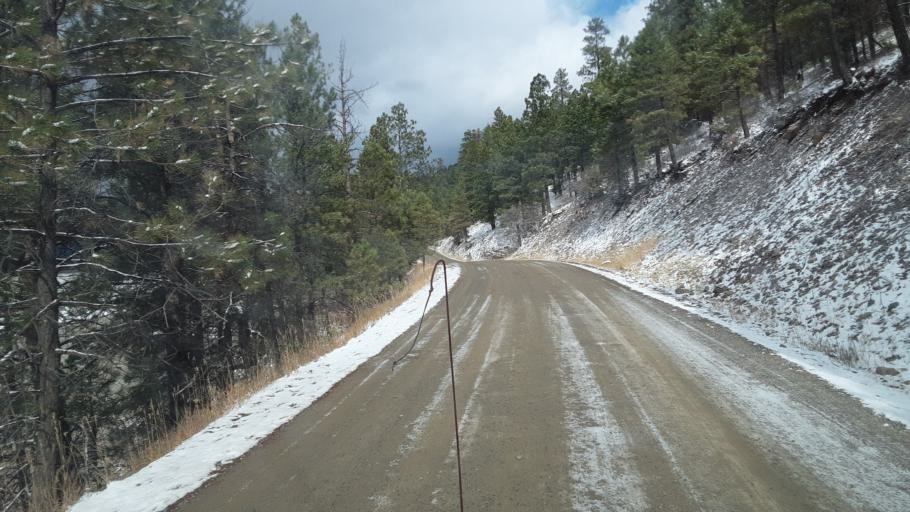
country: US
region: Colorado
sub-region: La Plata County
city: Bayfield
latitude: 37.4166
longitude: -107.5363
